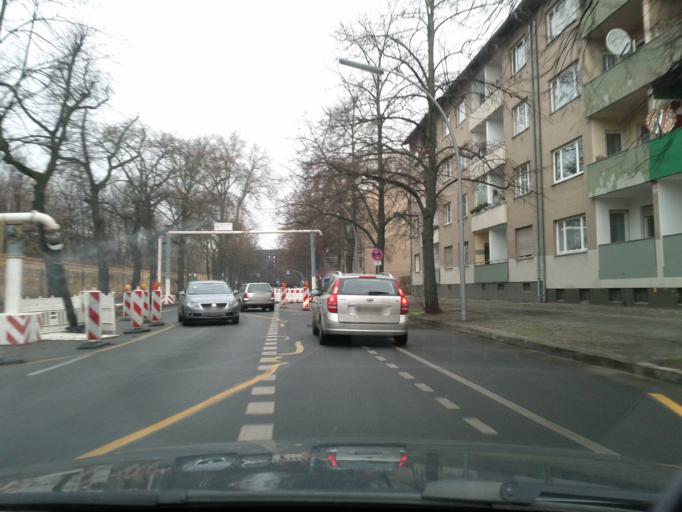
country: DE
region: Berlin
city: Gesundbrunnen
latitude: 52.5384
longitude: 13.3816
